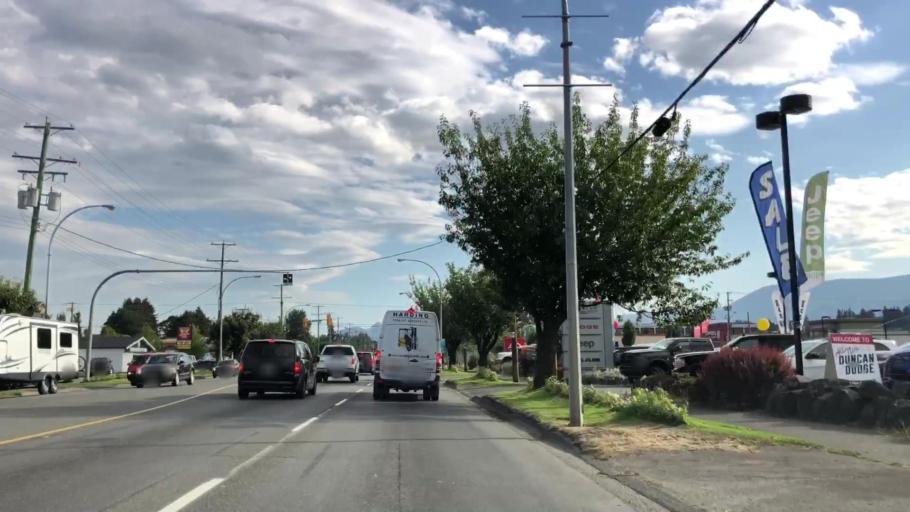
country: CA
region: British Columbia
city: Duncan
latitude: 48.7800
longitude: -123.6990
